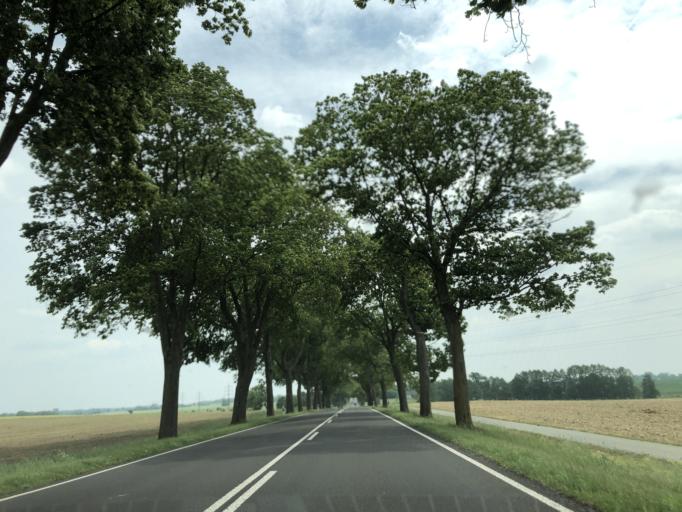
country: DE
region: Brandenburg
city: Kyritz
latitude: 52.9580
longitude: 12.3542
